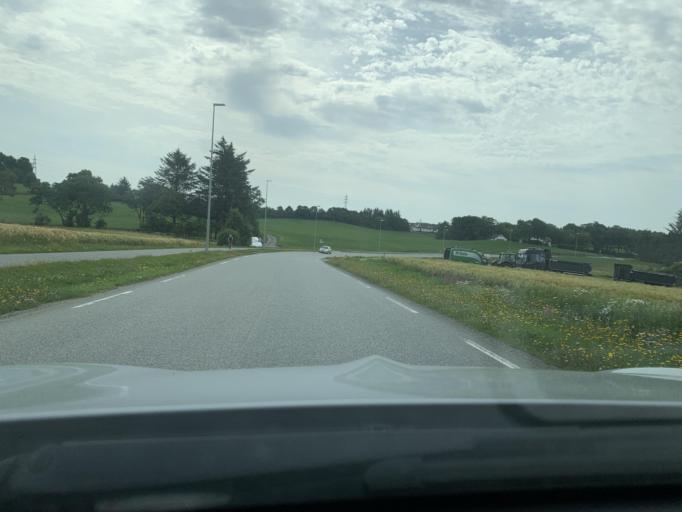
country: NO
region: Rogaland
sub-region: Time
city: Bryne
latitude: 58.7426
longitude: 5.6897
